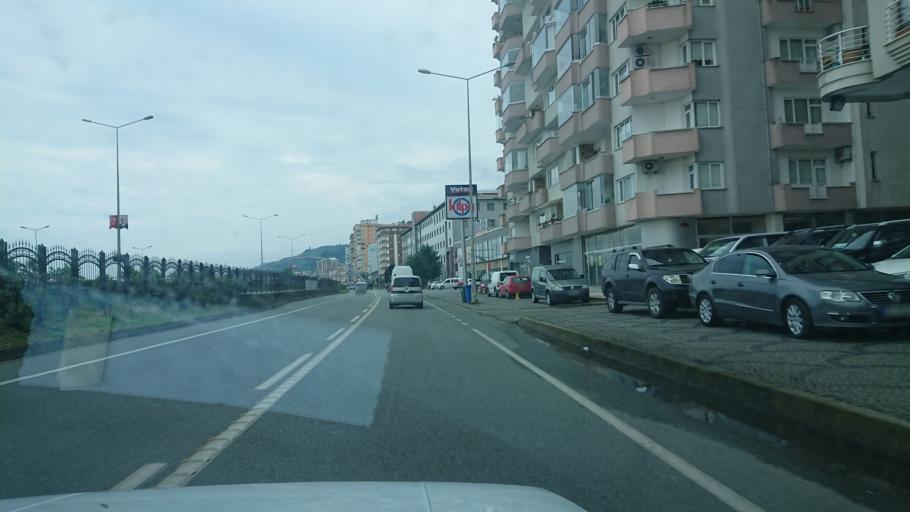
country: TR
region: Rize
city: Rize
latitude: 41.0256
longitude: 40.5359
